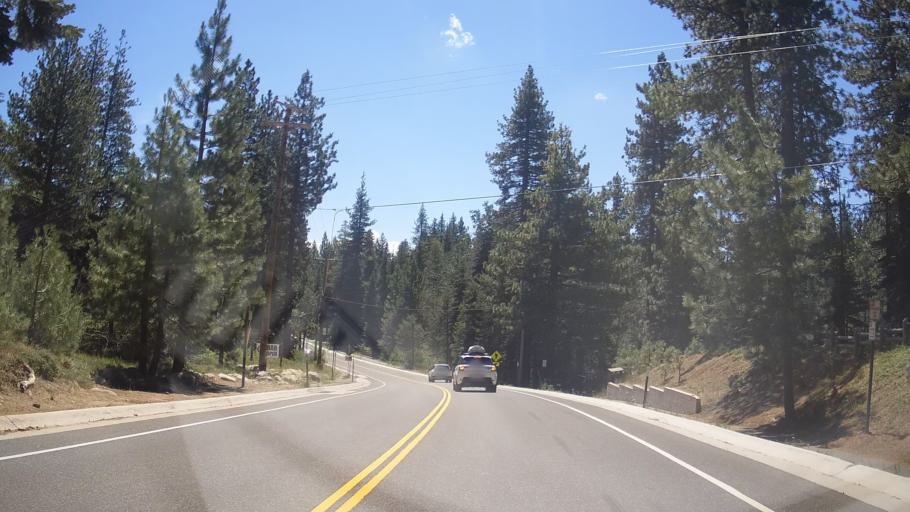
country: US
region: California
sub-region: Placer County
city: Tahoma
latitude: 39.0719
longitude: -120.1434
